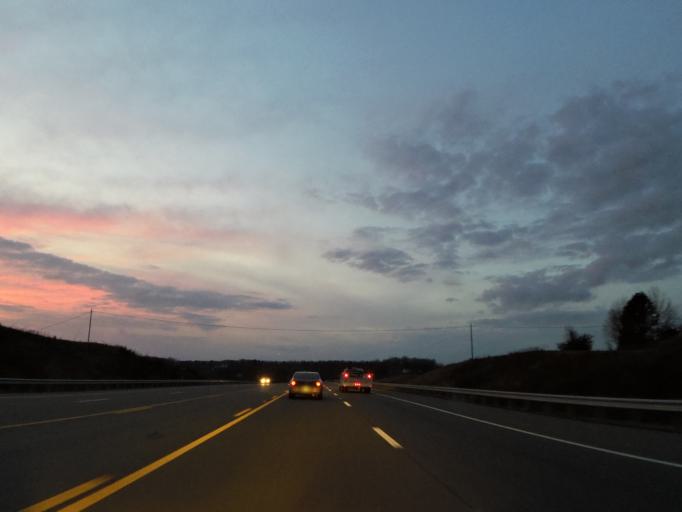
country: US
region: Tennessee
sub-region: Polk County
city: Benton
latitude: 35.1686
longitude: -84.6714
